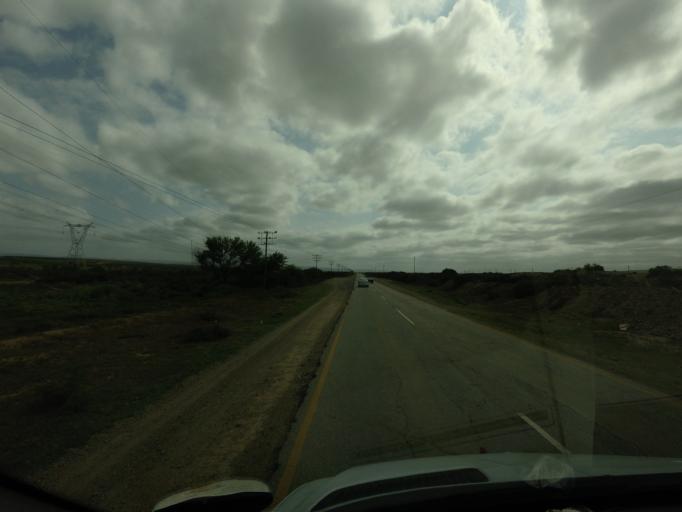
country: ZA
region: Eastern Cape
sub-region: Cacadu District Municipality
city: Kirkwood
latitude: -33.5018
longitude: 25.6961
